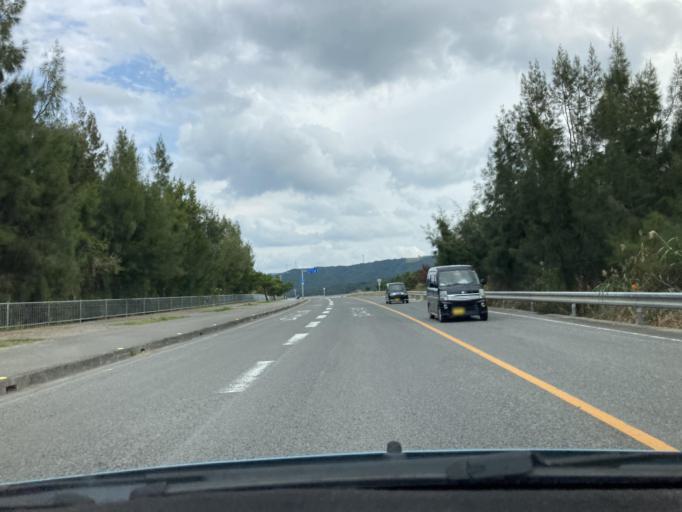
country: JP
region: Okinawa
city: Ishikawa
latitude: 26.4480
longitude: 127.8143
